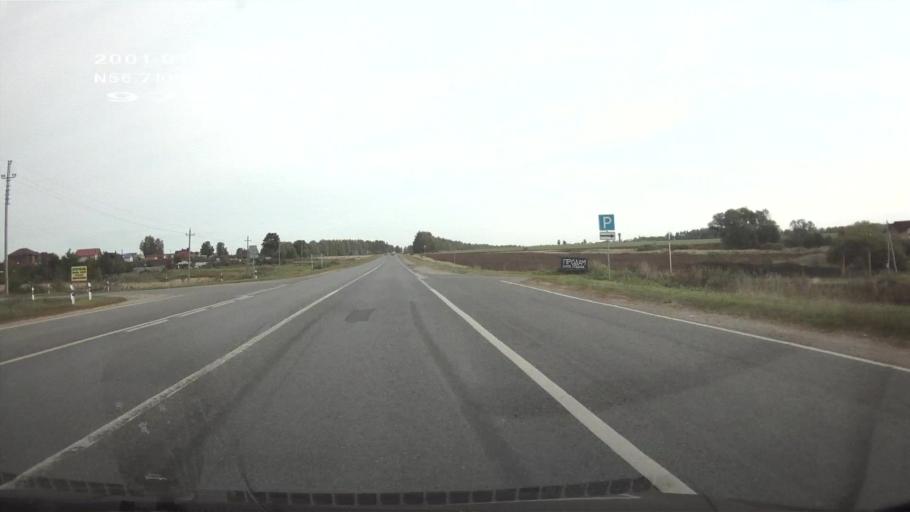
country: RU
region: Mariy-El
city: Yoshkar-Ola
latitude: 56.7109
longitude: 48.0861
